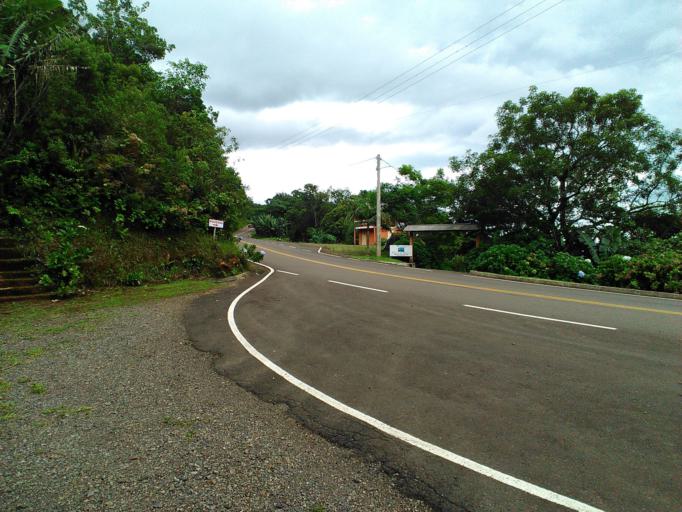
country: BR
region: Rio Grande do Sul
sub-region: Torres
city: Torres
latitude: -29.1863
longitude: -49.9883
